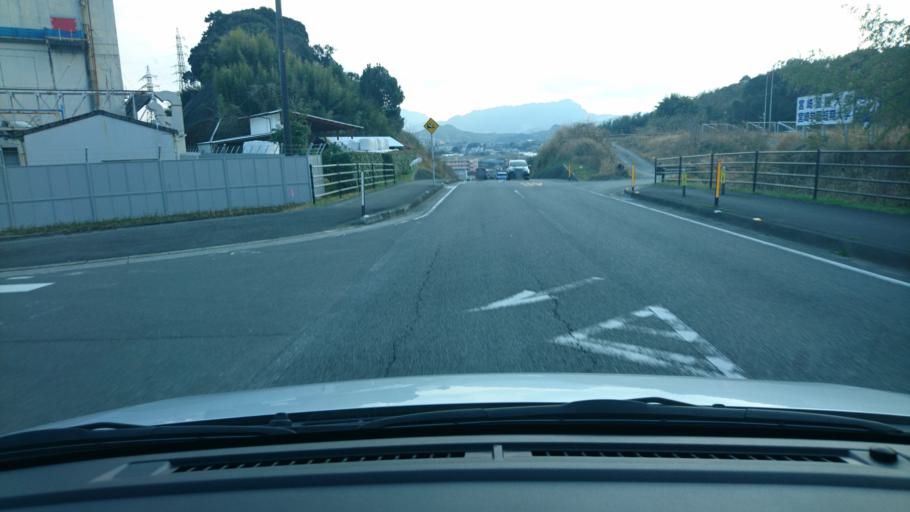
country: JP
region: Miyazaki
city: Miyazaki-shi
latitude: 31.8578
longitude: 131.3991
